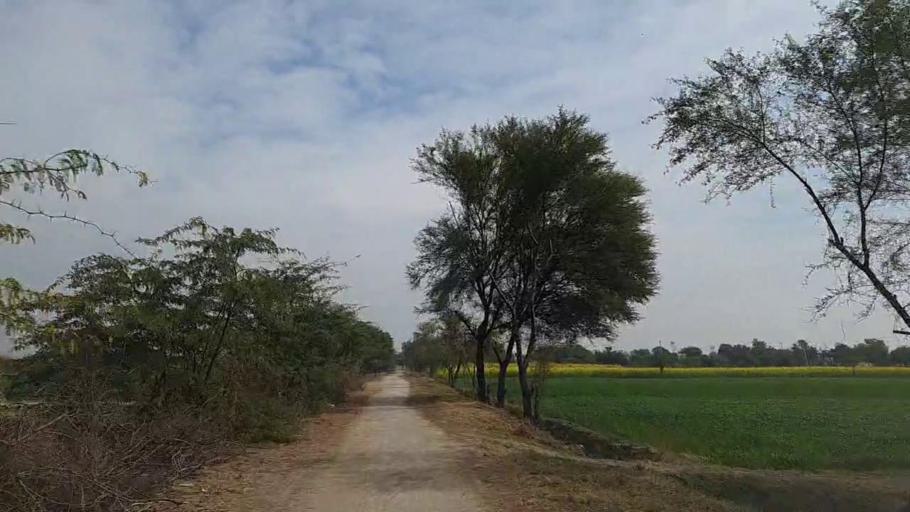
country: PK
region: Sindh
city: Nawabshah
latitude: 26.3761
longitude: 68.4428
